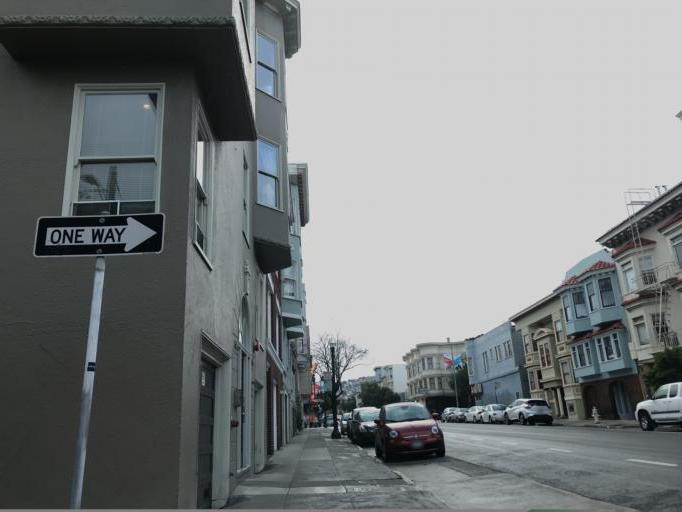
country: US
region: California
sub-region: San Francisco County
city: San Francisco
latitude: 37.7631
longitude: -122.4230
